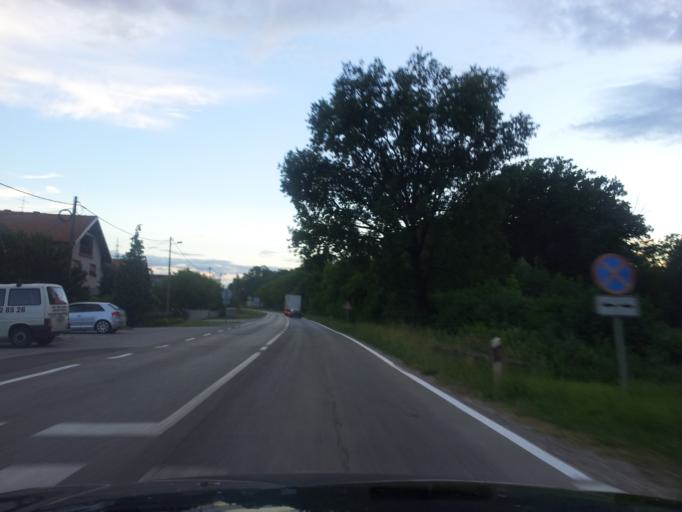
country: HR
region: Karlovacka
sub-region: Grad Karlovac
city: Karlovac
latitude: 45.5249
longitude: 15.5568
